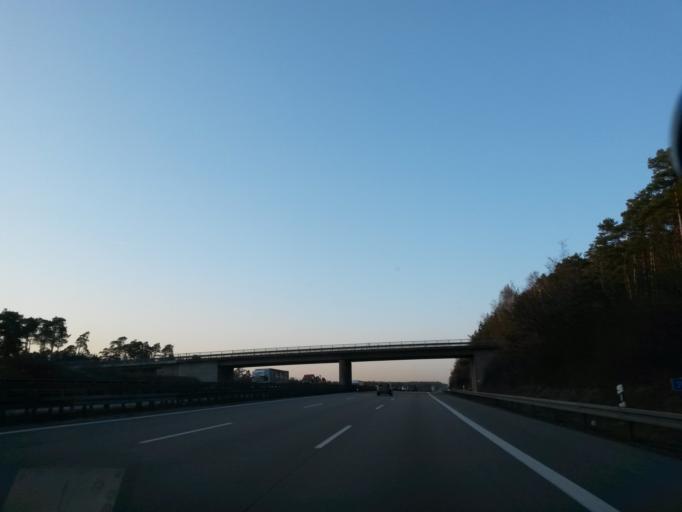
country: DE
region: Bavaria
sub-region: Regierungsbezirk Mittelfranken
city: Allersberg
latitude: 49.2785
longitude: 11.2097
